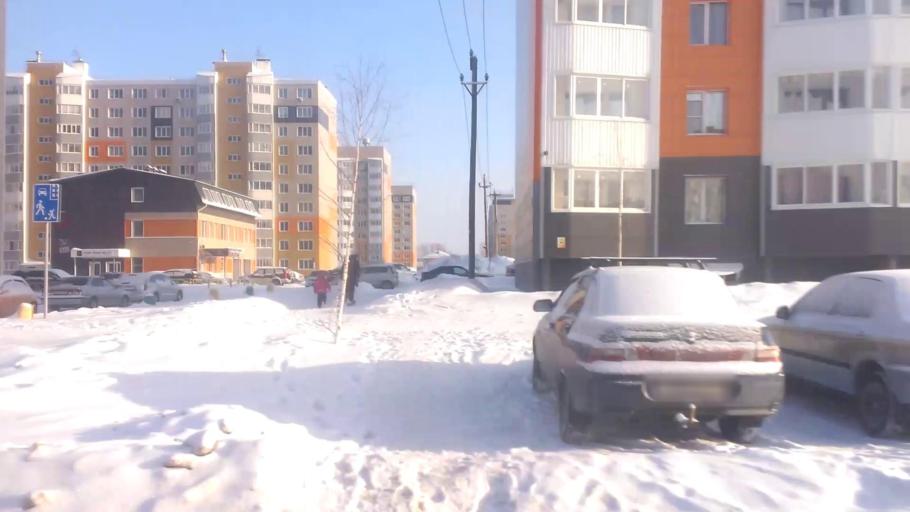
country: RU
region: Altai Krai
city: Novosilikatnyy
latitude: 53.3394
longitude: 83.6542
